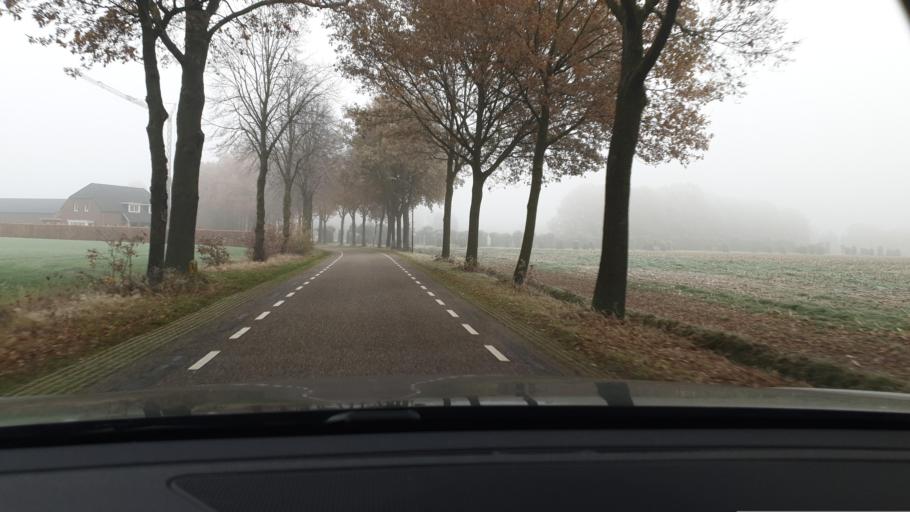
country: NL
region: North Brabant
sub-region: Gemeente Bladel en Netersel
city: Bladel
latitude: 51.3994
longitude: 5.2004
